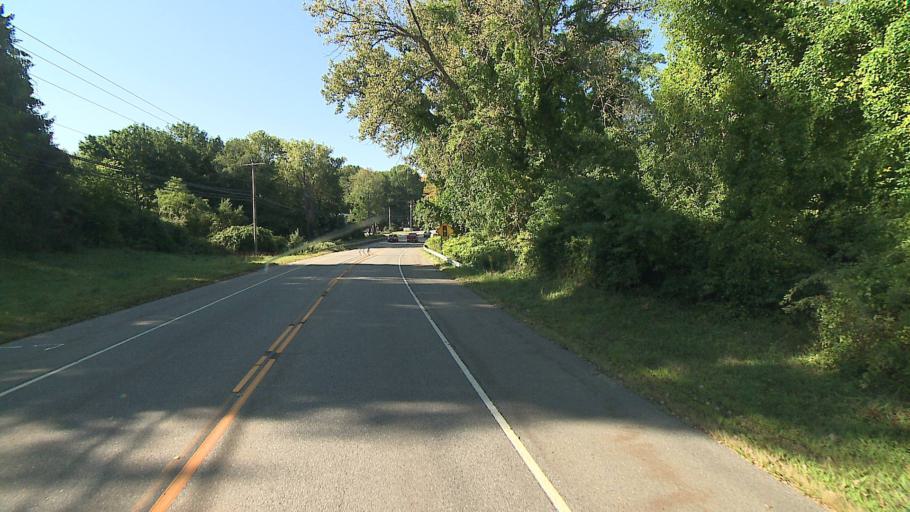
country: US
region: Connecticut
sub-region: New London County
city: Gales Ferry
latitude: 41.4440
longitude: -72.0774
